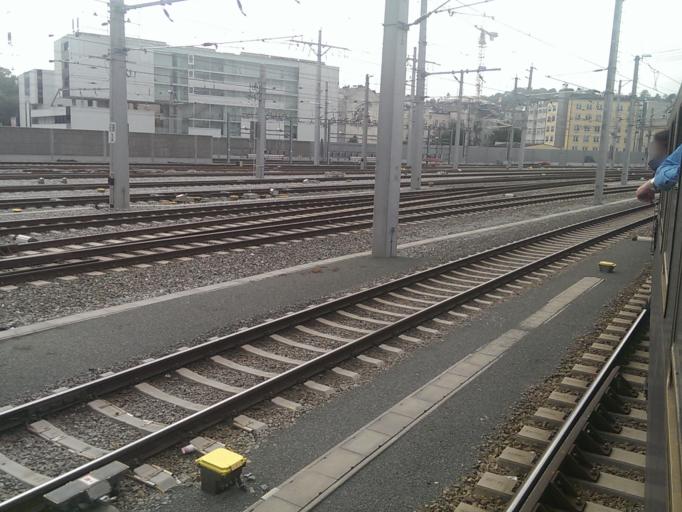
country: AT
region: Salzburg
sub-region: Salzburg Stadt
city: Salzburg
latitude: 47.8104
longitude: 13.0435
